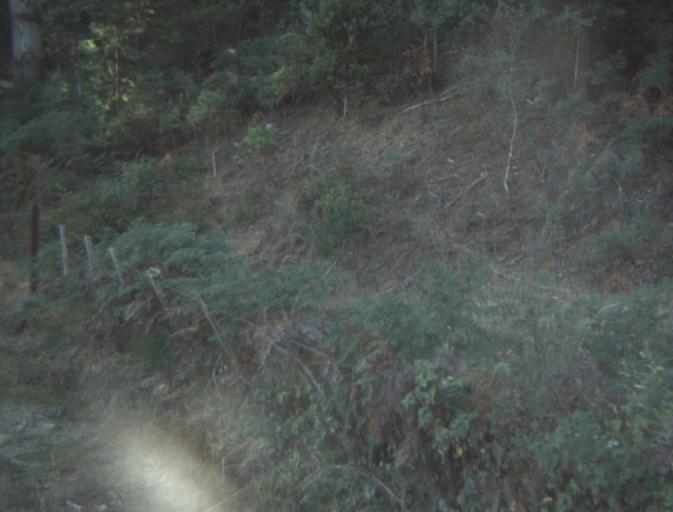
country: AU
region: Tasmania
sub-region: Launceston
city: Mayfield
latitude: -41.2884
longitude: 147.1973
